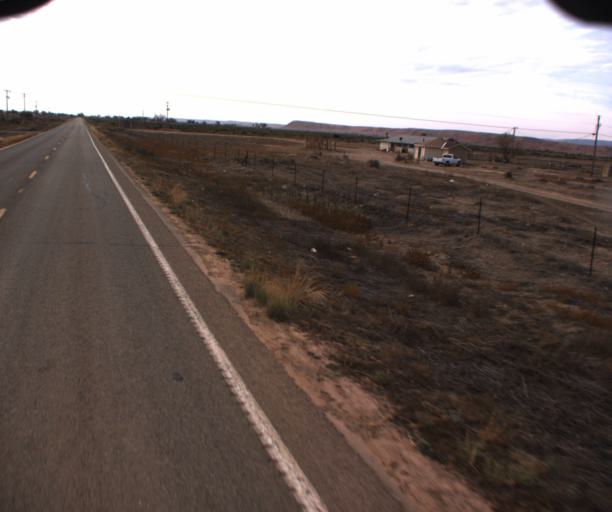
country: US
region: Arizona
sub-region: Apache County
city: Many Farms
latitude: 36.4362
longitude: -109.6071
